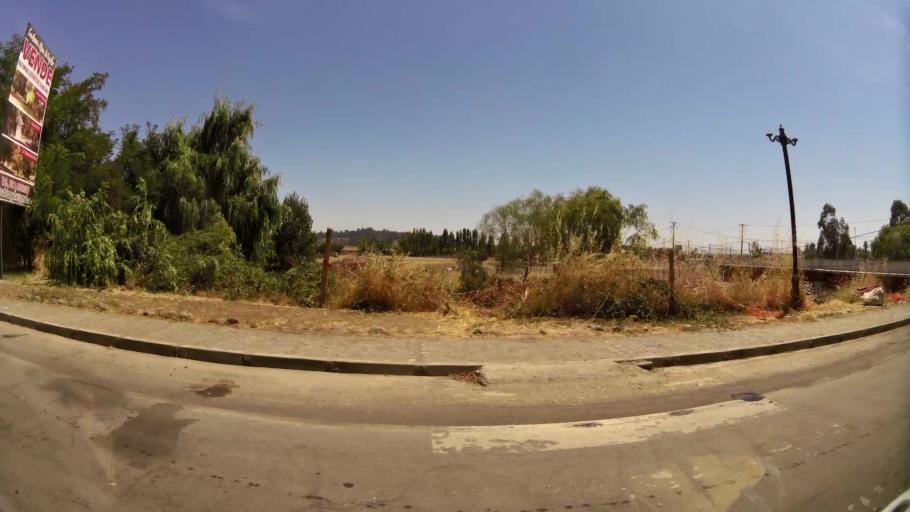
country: CL
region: Maule
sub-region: Provincia de Curico
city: Curico
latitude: -34.9907
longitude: -71.2101
